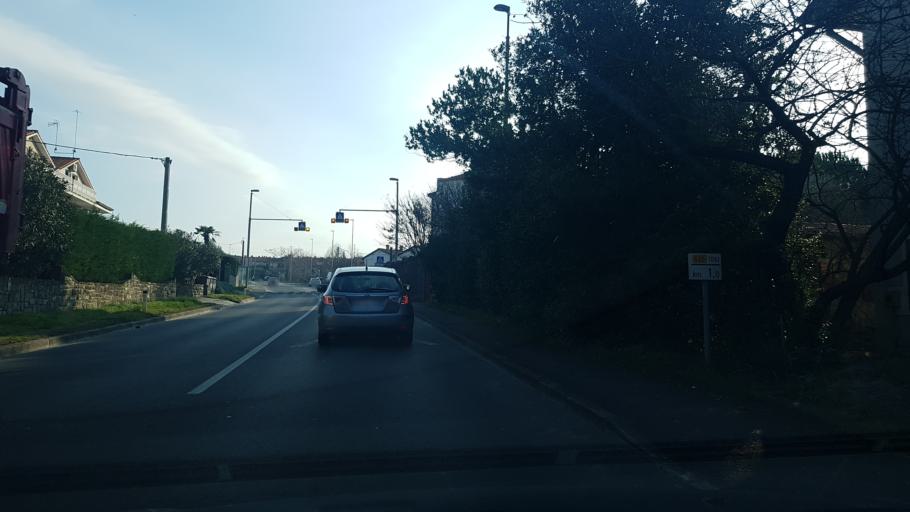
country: SI
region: Koper-Capodistria
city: Prade
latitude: 45.5409
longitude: 13.7706
